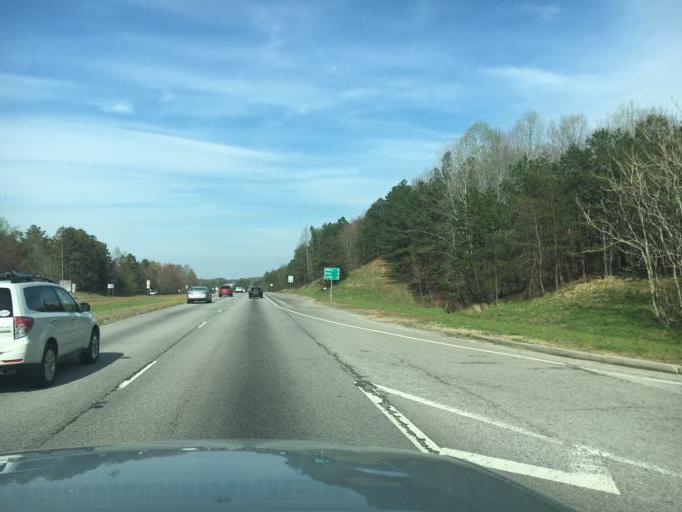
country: US
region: Georgia
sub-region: Hall County
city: Lula
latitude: 34.3955
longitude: -83.6901
